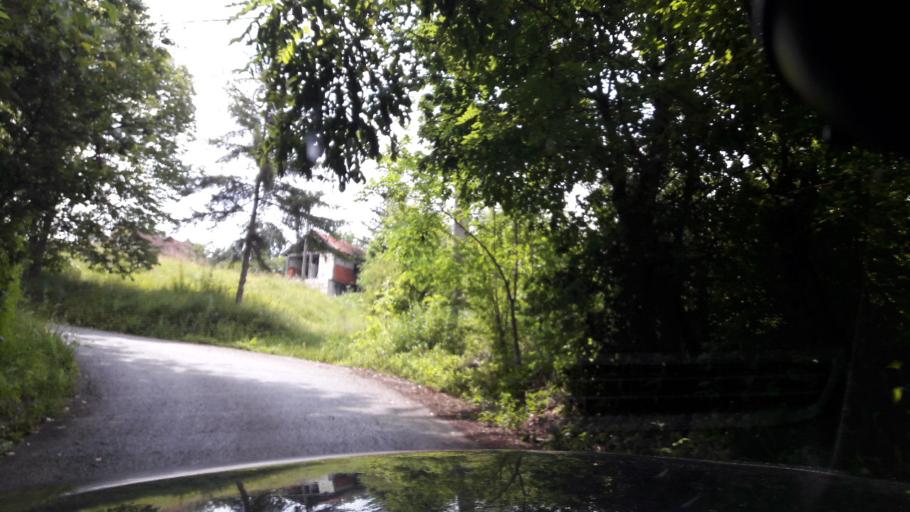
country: RS
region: Central Serbia
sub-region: Belgrade
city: Sopot
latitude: 44.6236
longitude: 20.5997
